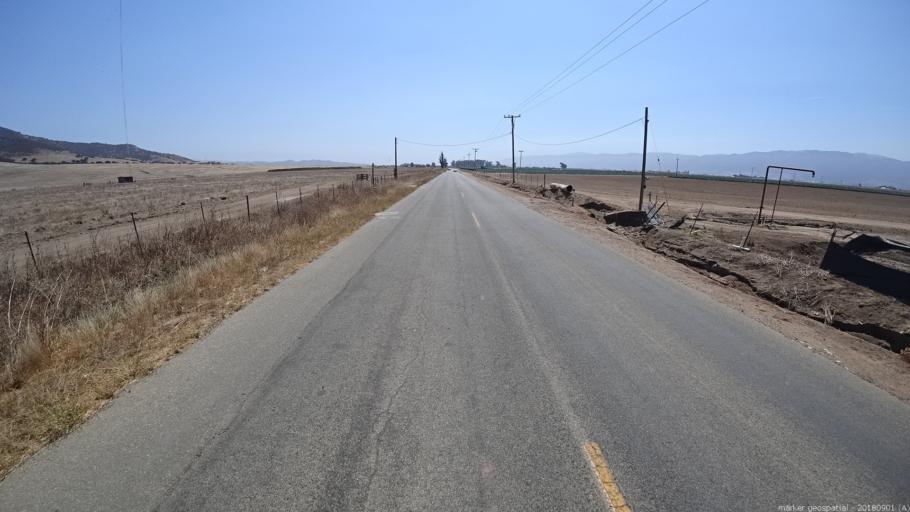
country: US
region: California
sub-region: Monterey County
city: Chualar
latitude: 36.6598
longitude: -121.5464
